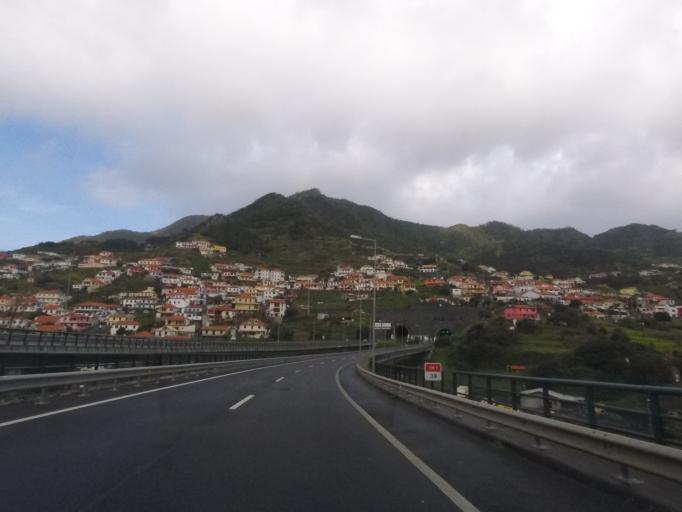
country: PT
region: Madeira
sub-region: Machico
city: Machico
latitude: 32.7313
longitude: -16.7779
